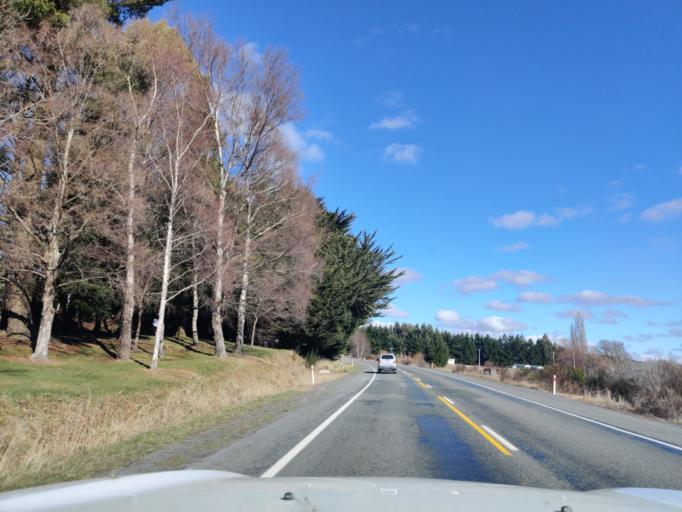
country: NZ
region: Manawatu-Wanganui
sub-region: Ruapehu District
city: Waiouru
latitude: -39.4722
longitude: 175.6693
